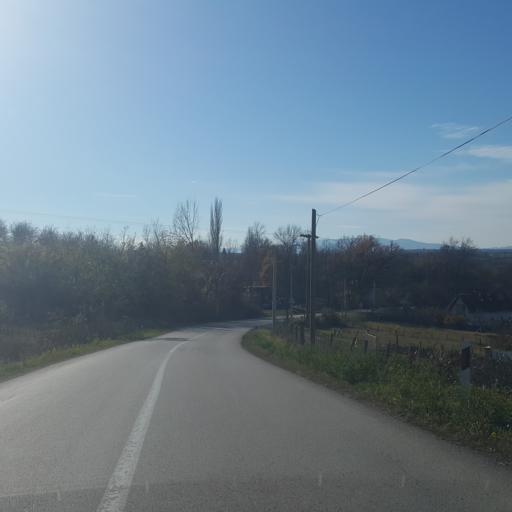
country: RS
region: Central Serbia
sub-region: Sumadijski Okrug
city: Raca
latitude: 44.2387
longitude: 20.8386
